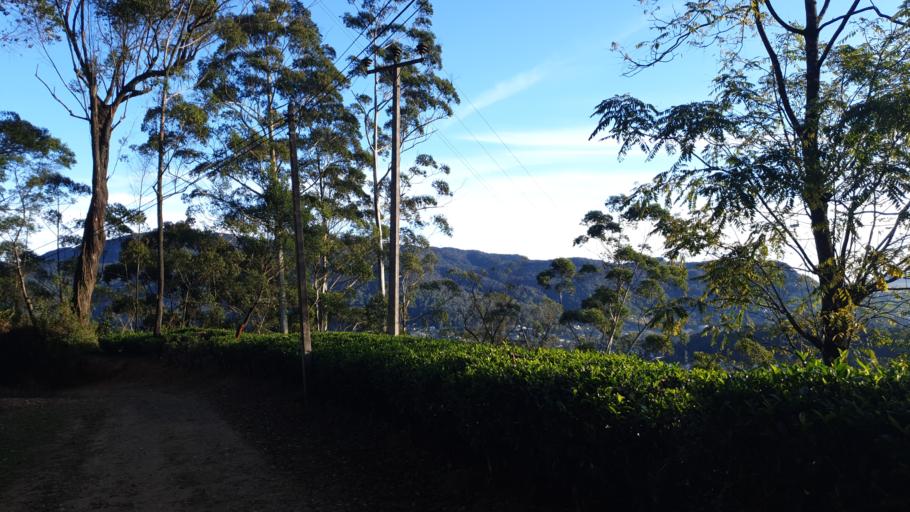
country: LK
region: Central
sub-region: Nuwara Eliya District
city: Nuwara Eliya
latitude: 6.9579
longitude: 80.7631
